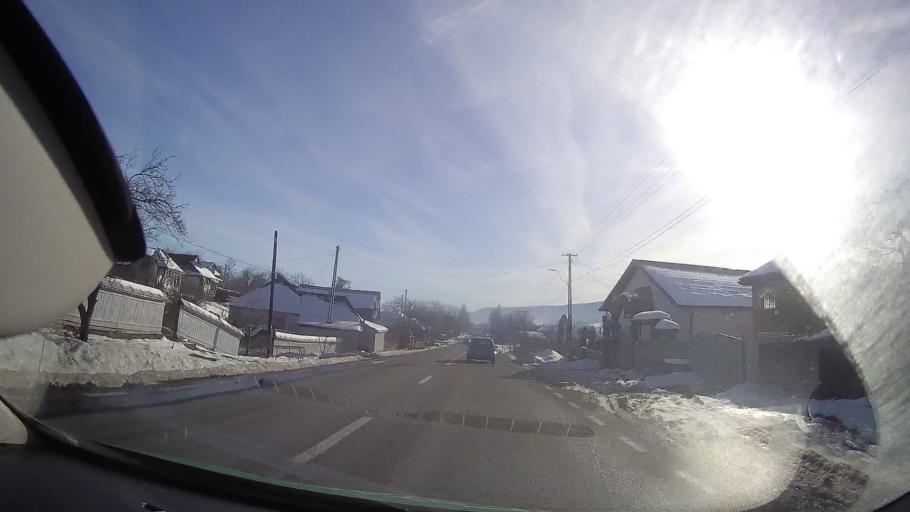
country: RO
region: Neamt
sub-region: Comuna Cracaoani
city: Cracaoani
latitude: 47.1010
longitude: 26.3083
